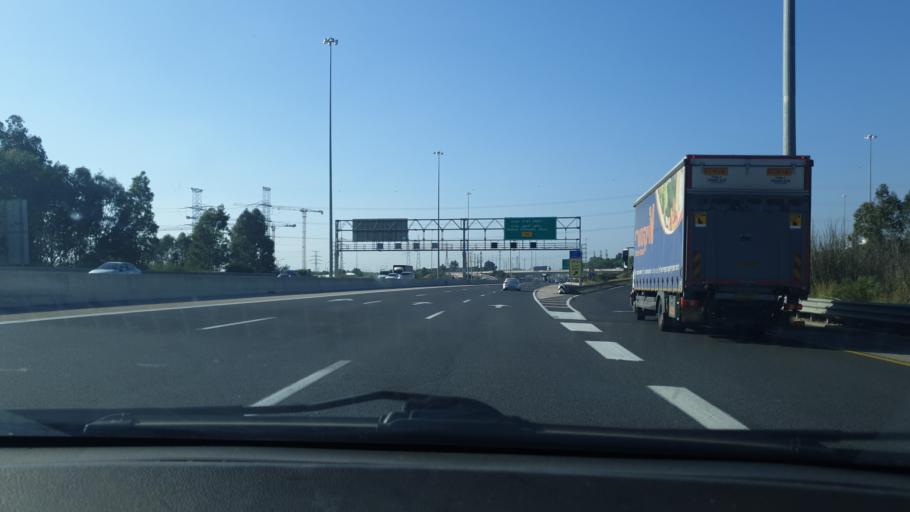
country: IL
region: Central District
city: Rishon LeZiyyon
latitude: 31.9551
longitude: 34.7800
